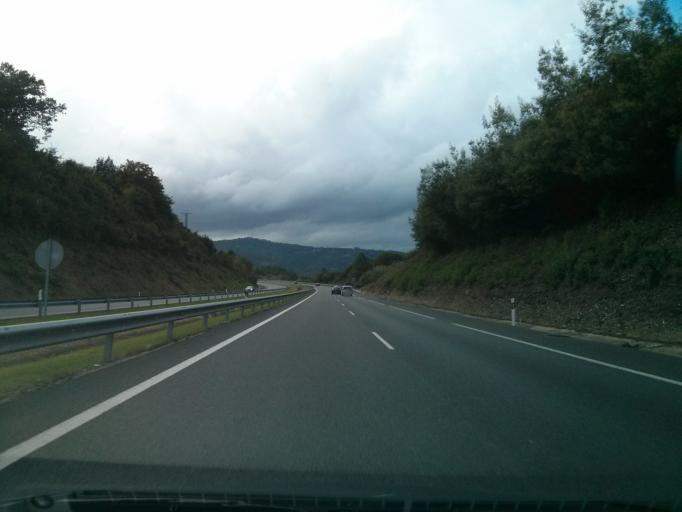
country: ES
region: Galicia
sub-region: Provincia de Ourense
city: Toen
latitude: 42.3331
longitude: -7.9657
